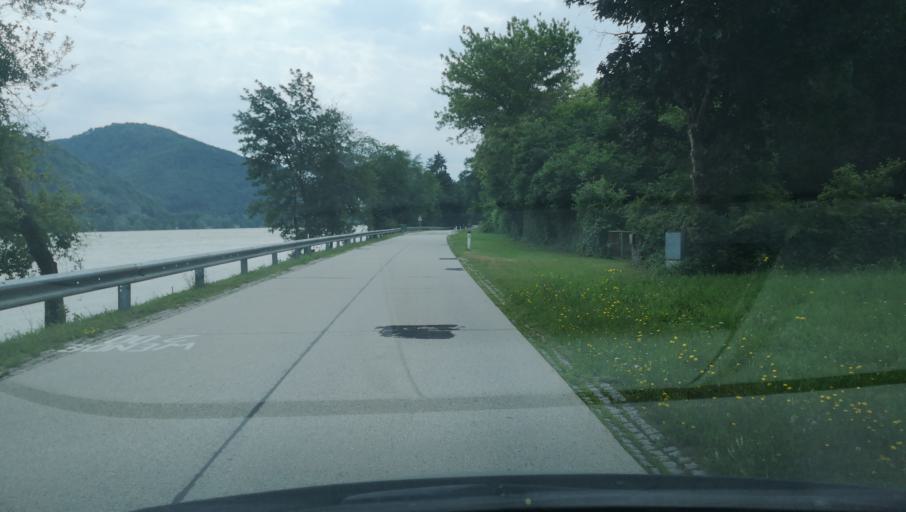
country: AT
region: Lower Austria
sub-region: Politischer Bezirk Melk
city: Nochling
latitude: 48.1947
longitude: 14.9858
